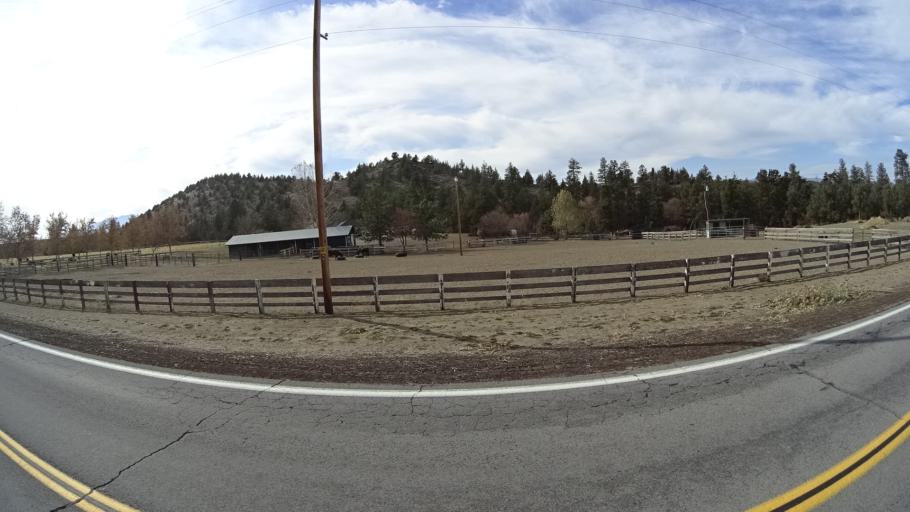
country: US
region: California
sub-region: Siskiyou County
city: Weed
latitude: 41.5476
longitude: -122.3754
